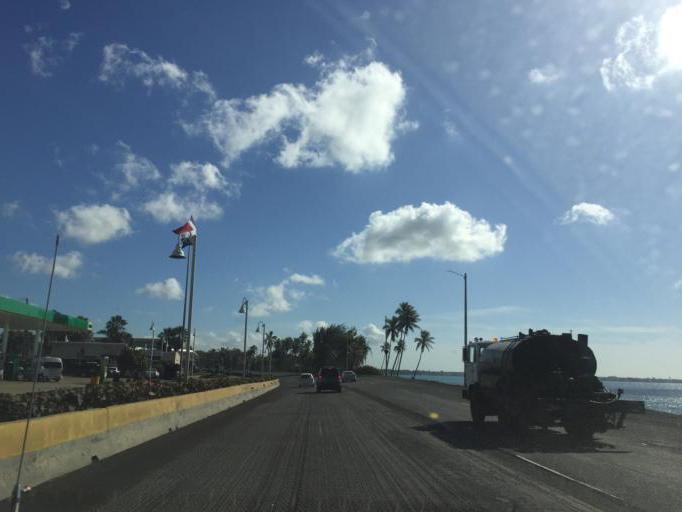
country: DO
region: Santo Domingo
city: Guerra
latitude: 18.4555
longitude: -69.7099
